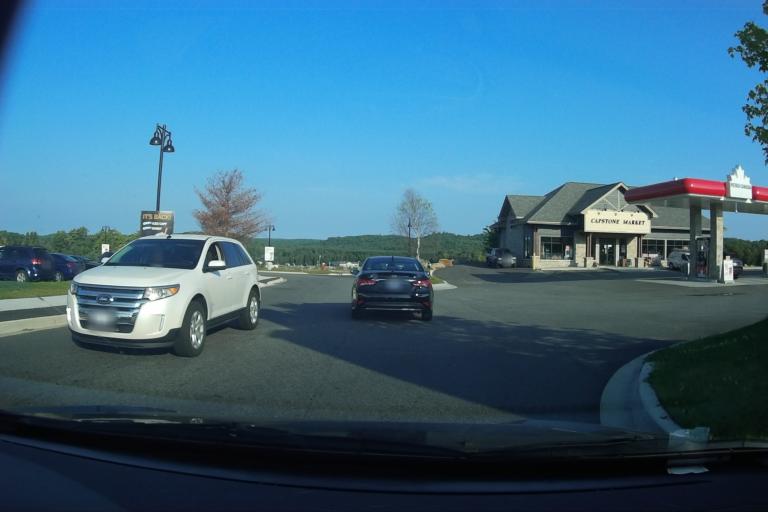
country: CA
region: Ontario
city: Huntsville
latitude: 45.3404
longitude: -79.2224
